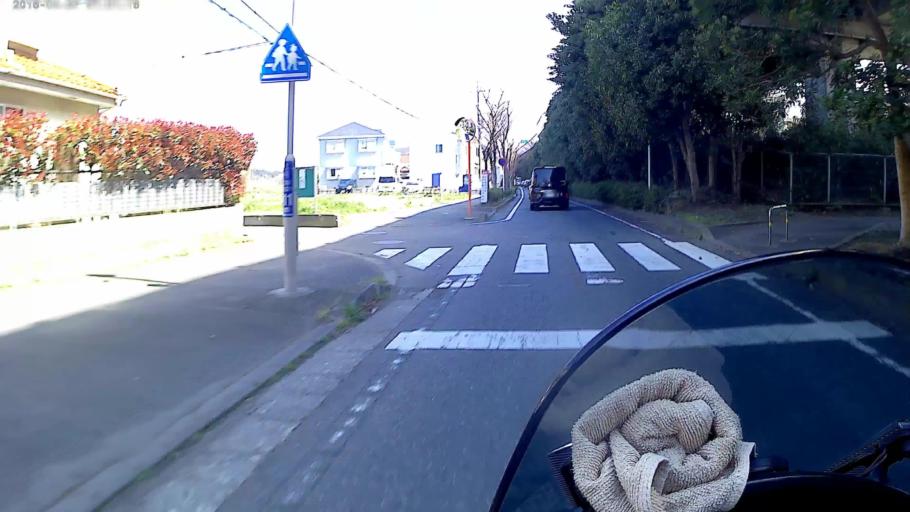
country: JP
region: Kanagawa
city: Chigasaki
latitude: 35.3480
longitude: 139.4236
